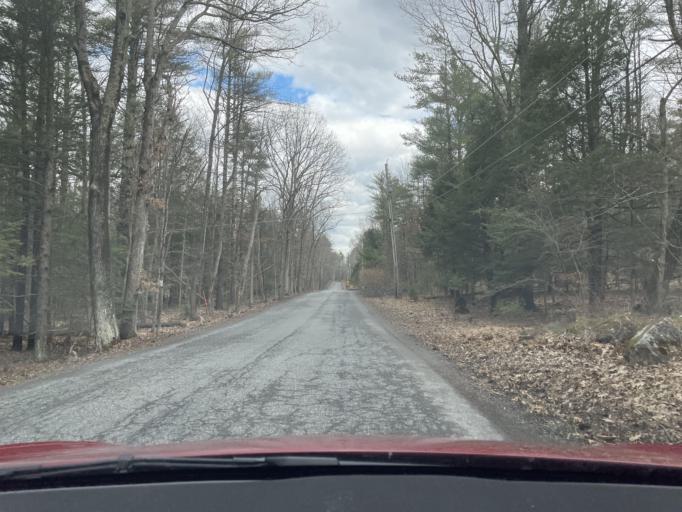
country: US
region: New York
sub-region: Ulster County
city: Zena
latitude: 42.0677
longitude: -74.0349
